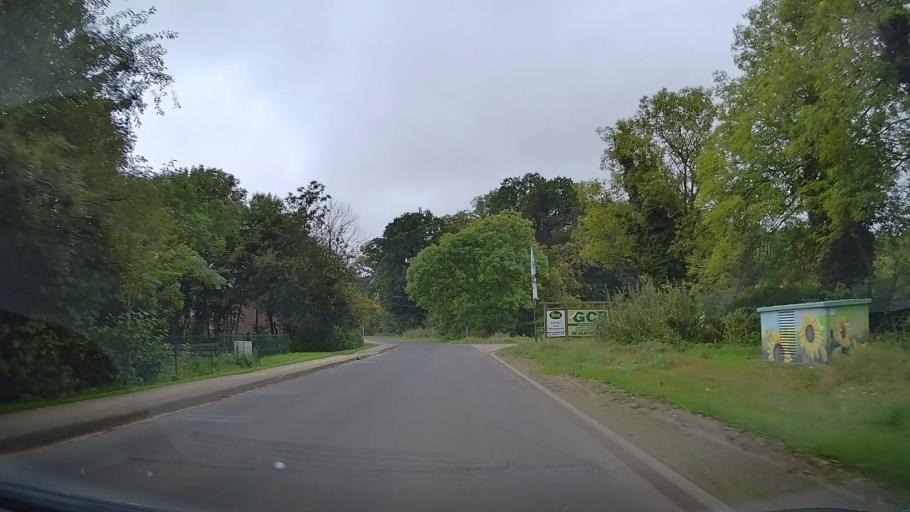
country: DE
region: Mecklenburg-Vorpommern
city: Tarnow
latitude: 53.7845
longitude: 12.0853
